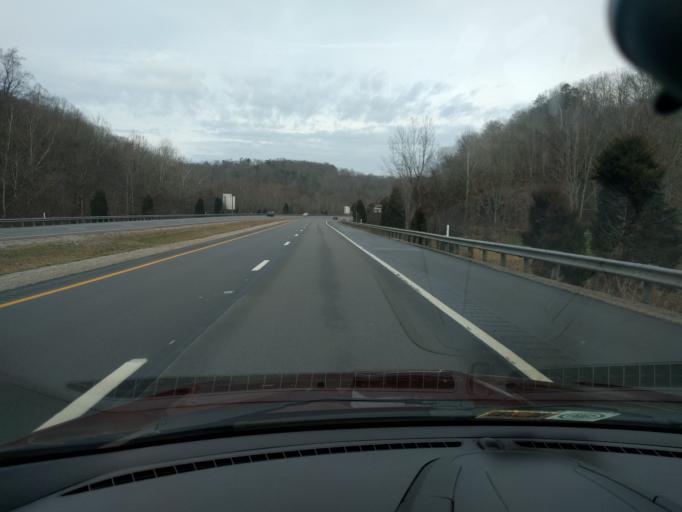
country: US
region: West Virginia
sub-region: Jackson County
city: Ripley
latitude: 38.7667
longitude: -81.7133
